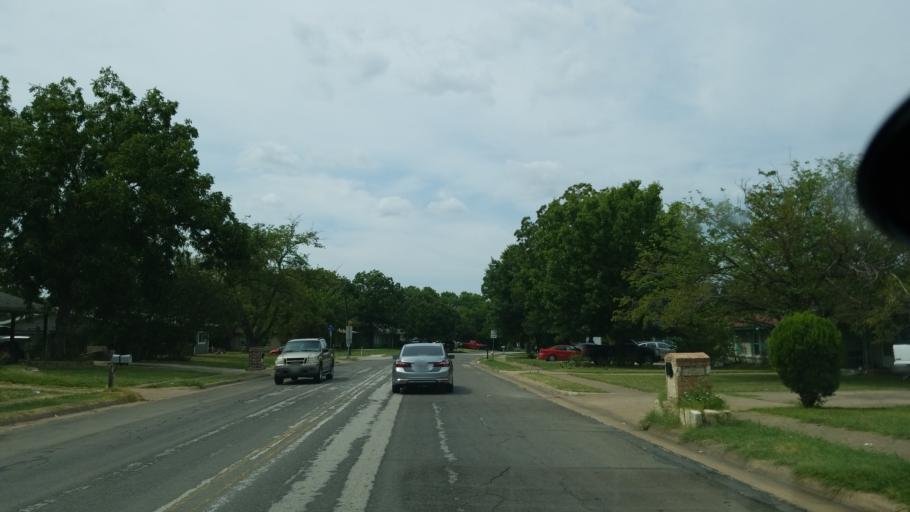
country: US
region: Texas
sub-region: Tarrant County
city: Arlington
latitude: 32.7321
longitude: -97.0840
